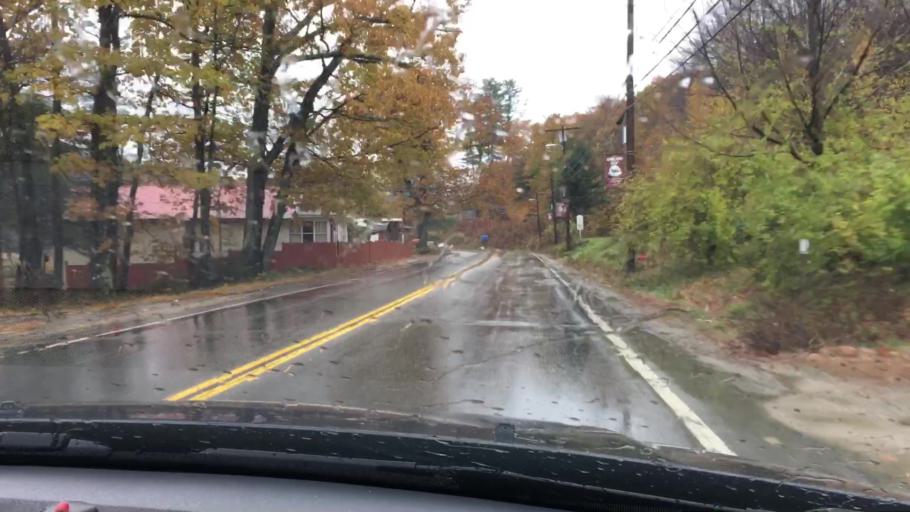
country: US
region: New Hampshire
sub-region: Grafton County
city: Ashland
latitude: 43.7023
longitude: -71.6305
